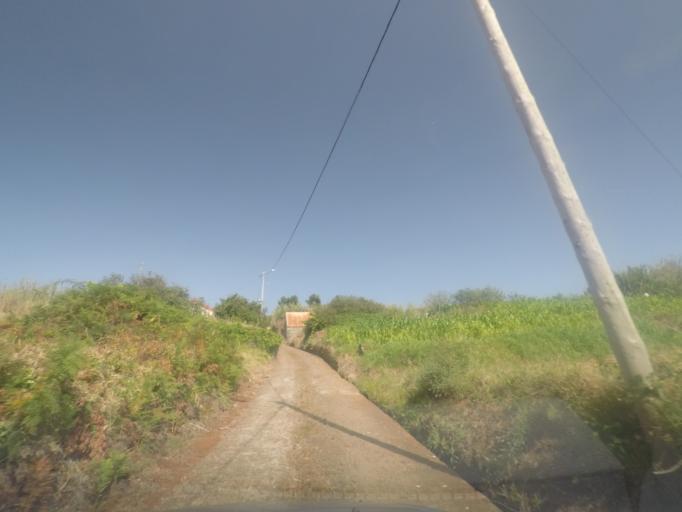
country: PT
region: Madeira
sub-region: Calheta
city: Faja da Ovelha
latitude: 32.8076
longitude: -17.2483
